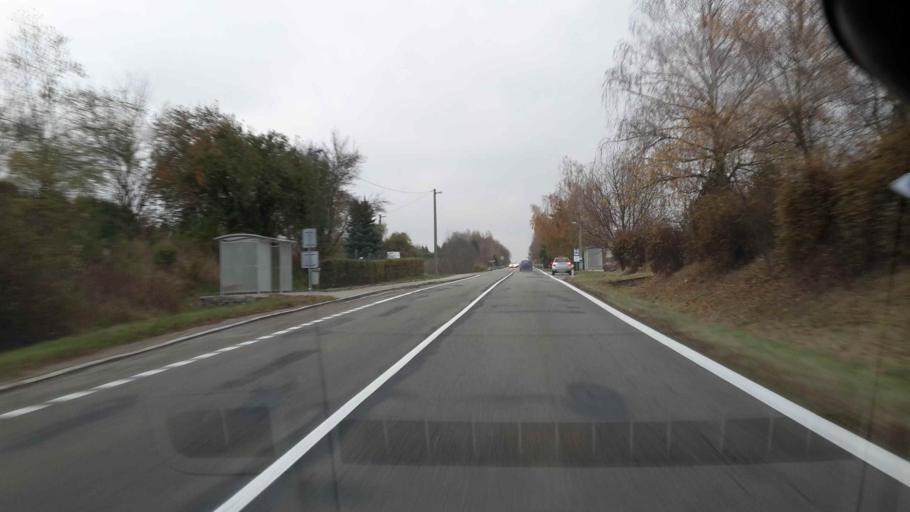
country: CZ
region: South Moravian
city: Lipuvka
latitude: 49.3335
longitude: 16.5735
